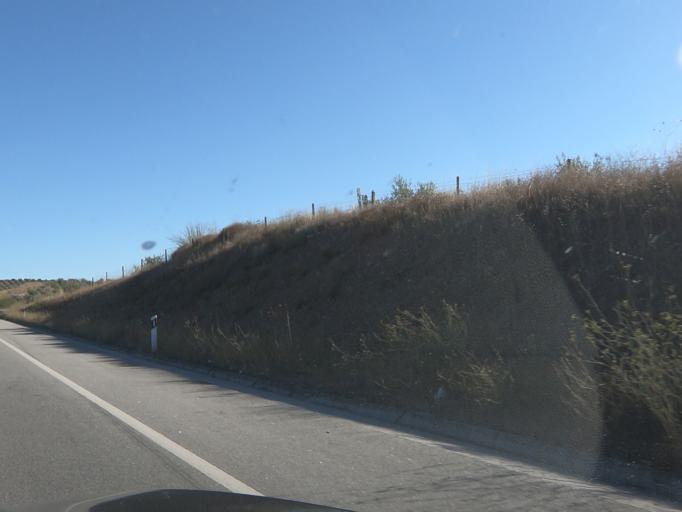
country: PT
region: Vila Real
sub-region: Valpacos
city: Valpacos
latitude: 41.5581
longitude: -7.2630
